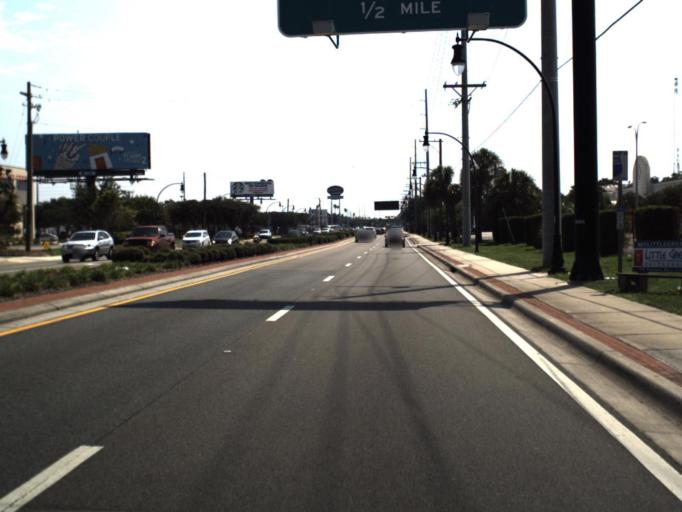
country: US
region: Florida
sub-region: Hillsborough County
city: Tampa
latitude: 27.8937
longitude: -82.5153
